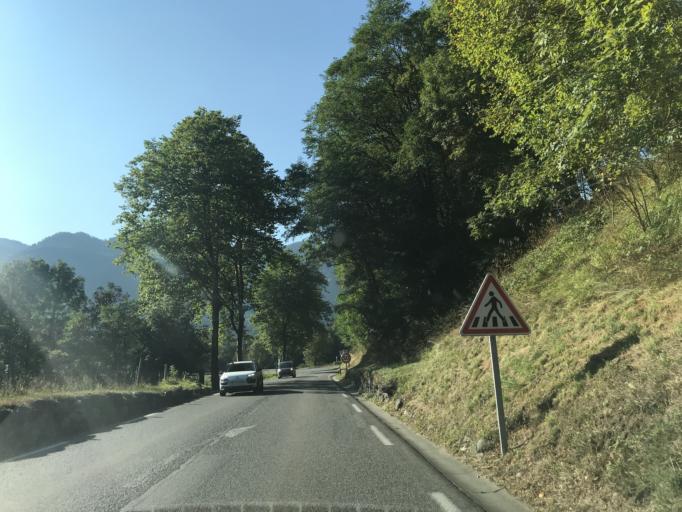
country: FR
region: Midi-Pyrenees
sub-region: Departement des Hautes-Pyrenees
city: Saint-Lary-Soulan
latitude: 42.8579
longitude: 0.3406
